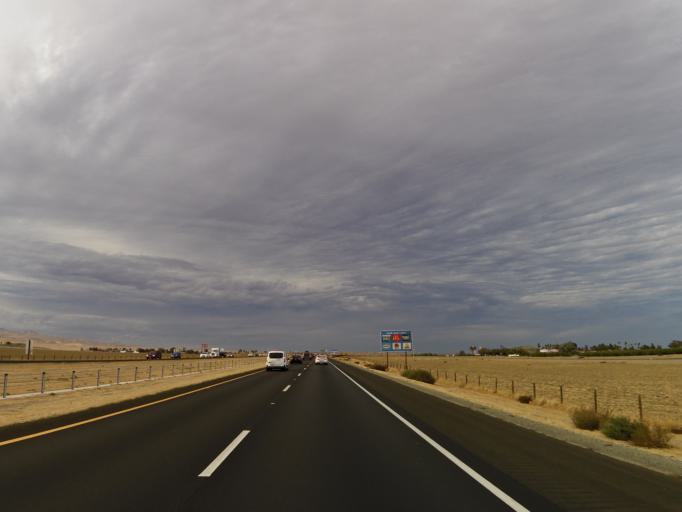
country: US
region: California
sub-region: Fresno County
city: Huron
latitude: 36.2451
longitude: -120.2379
